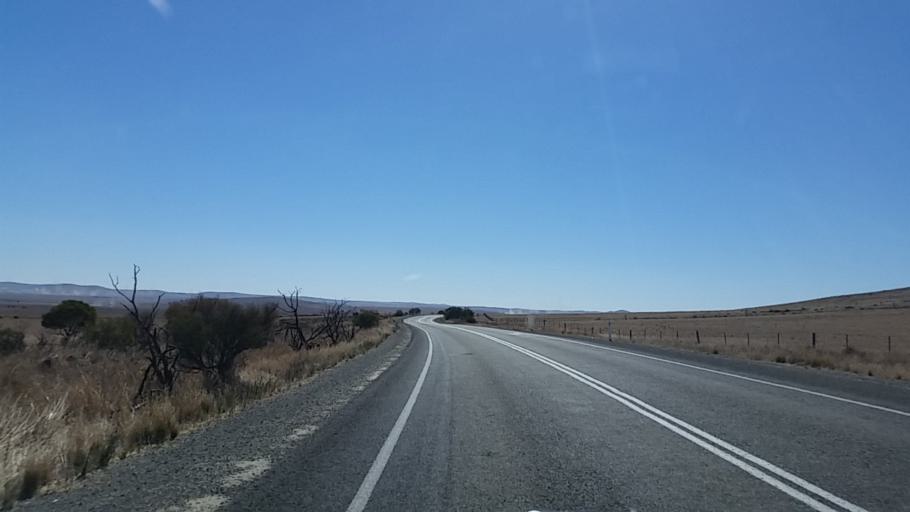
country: AU
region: South Australia
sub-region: Northern Areas
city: Jamestown
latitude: -33.3269
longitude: 138.8876
